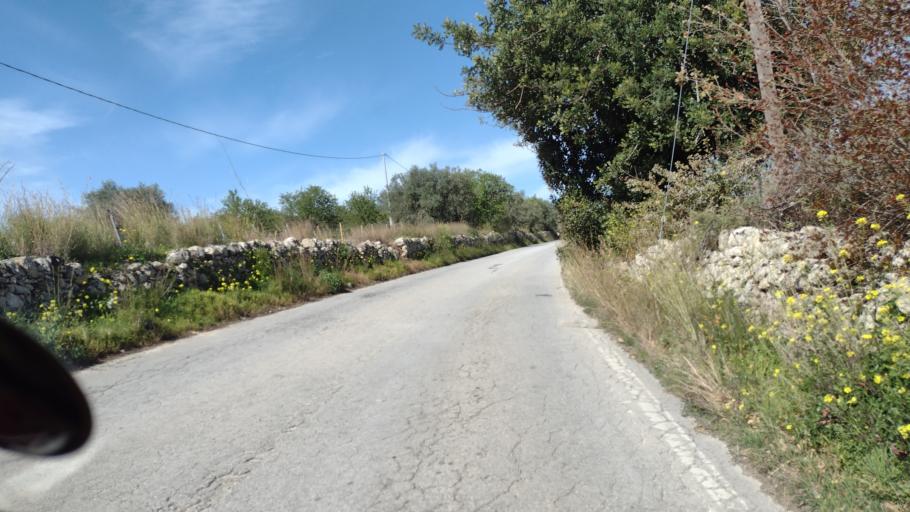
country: IT
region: Sicily
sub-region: Provincia di Siracusa
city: Noto
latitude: 36.8869
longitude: 15.0539
